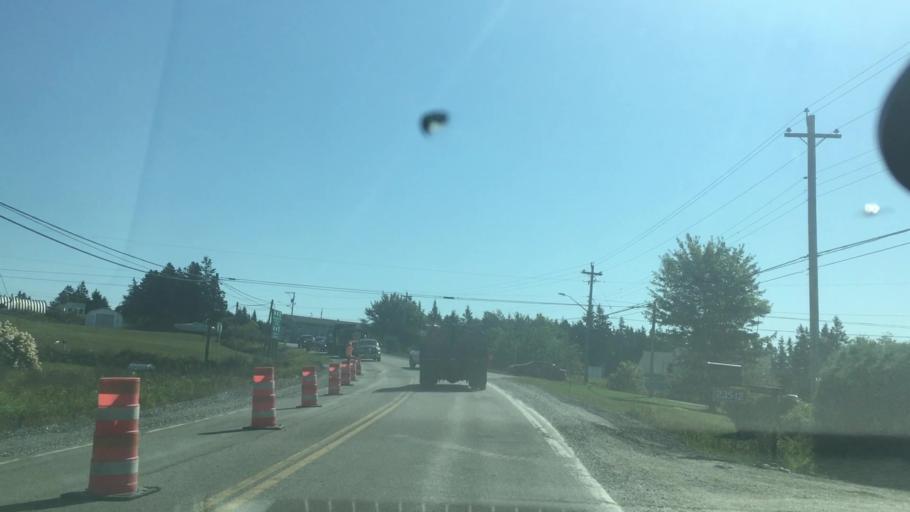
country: CA
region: Nova Scotia
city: New Glasgow
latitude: 44.9056
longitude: -62.4892
